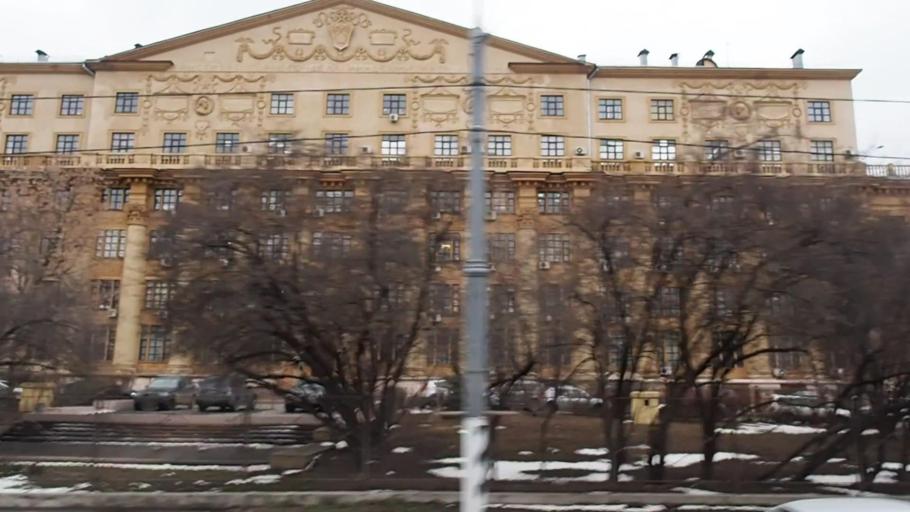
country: RU
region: Moskovskaya
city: Leninskiye Gory
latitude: 55.6983
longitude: 37.5732
